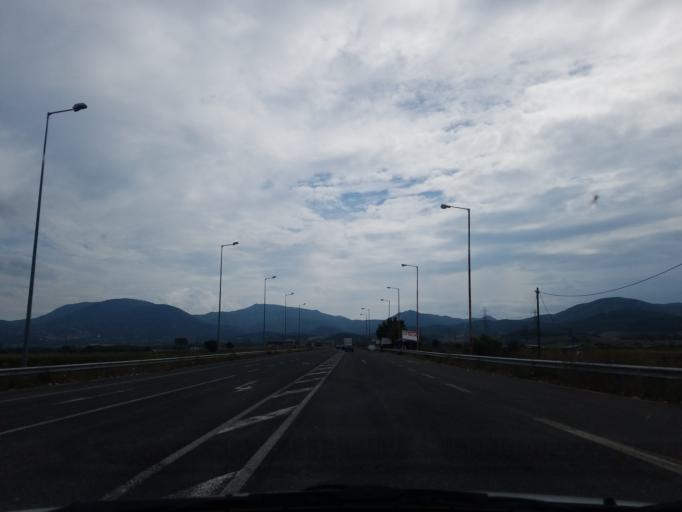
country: GR
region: Central Greece
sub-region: Nomos Fthiotidos
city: Domokos
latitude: 39.0424
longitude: 22.3523
